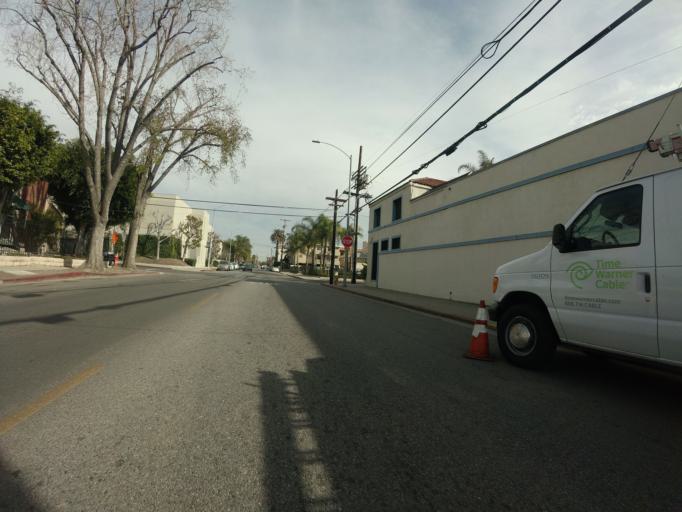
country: US
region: California
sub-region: Los Angeles County
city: Hollywood
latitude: 34.0871
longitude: -118.3334
